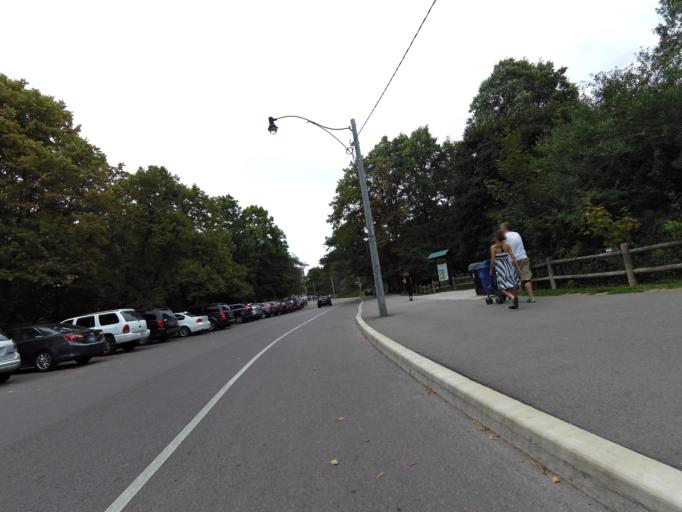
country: CA
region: Ontario
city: Toronto
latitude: 43.6471
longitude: -79.4649
